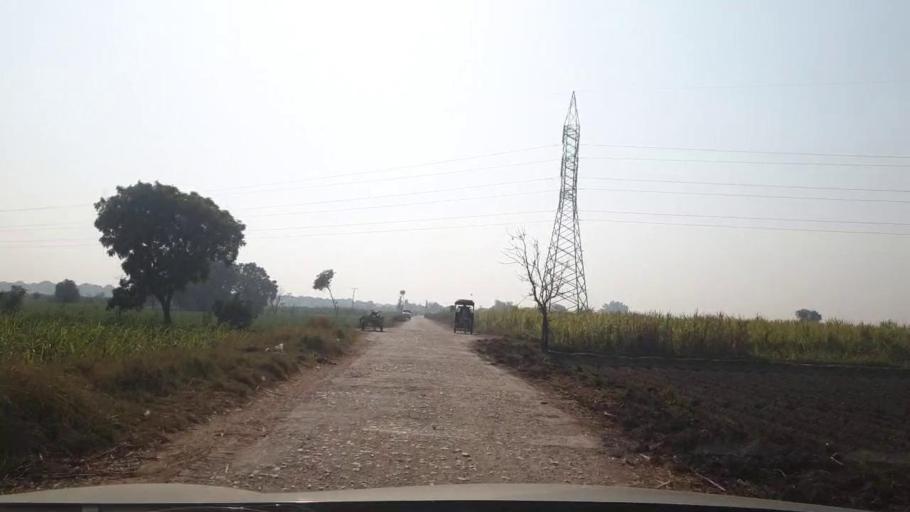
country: PK
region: Sindh
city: Tando Allahyar
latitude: 25.4939
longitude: 68.7540
